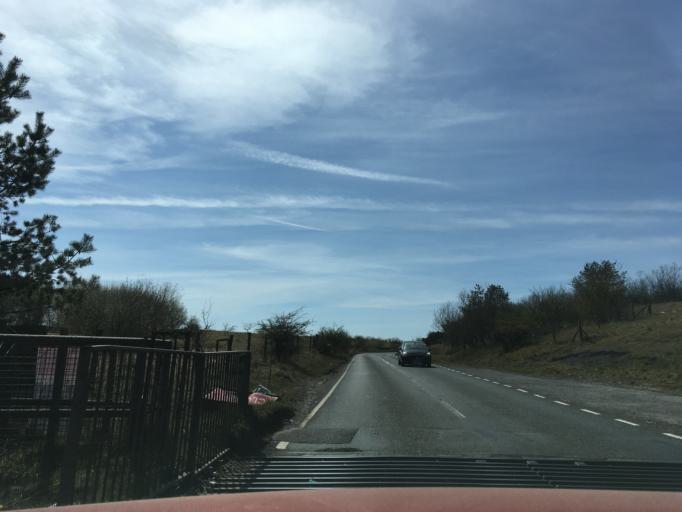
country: GB
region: Wales
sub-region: Caerphilly County Borough
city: Rhymney
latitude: 51.7696
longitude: -3.3288
